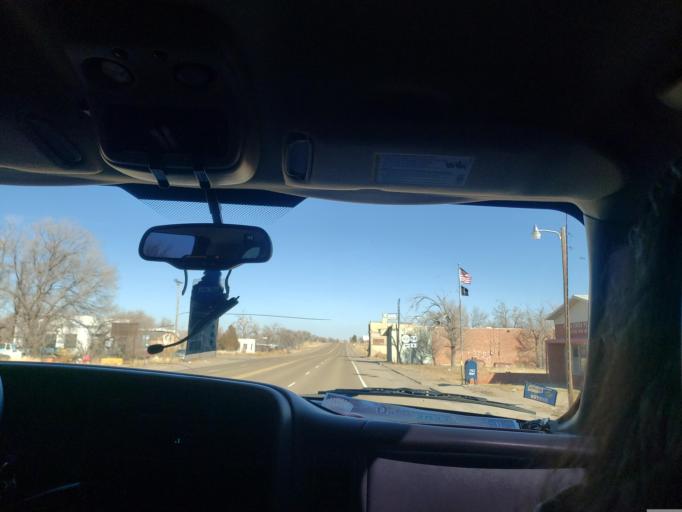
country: US
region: New Mexico
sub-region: Quay County
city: Logan
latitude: 35.6072
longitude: -103.1007
